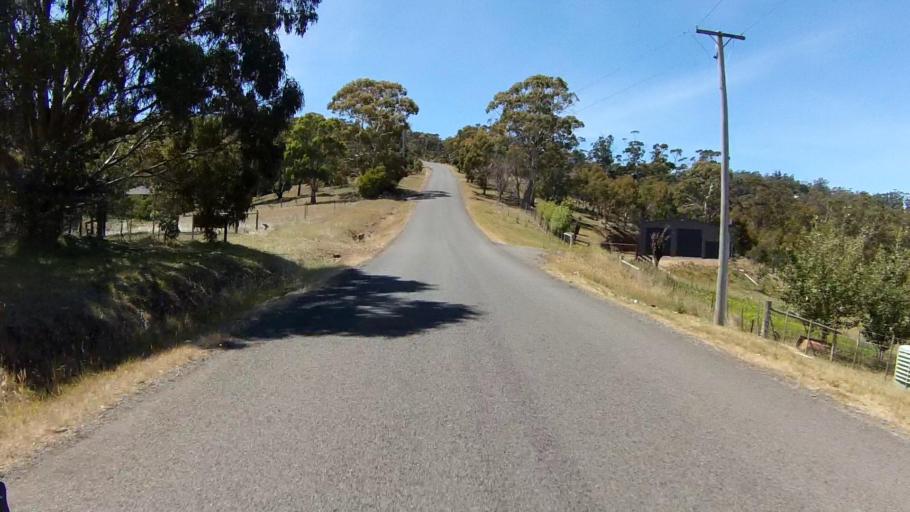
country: AU
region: Tasmania
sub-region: Clarence
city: Cambridge
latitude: -42.8506
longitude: 147.4264
